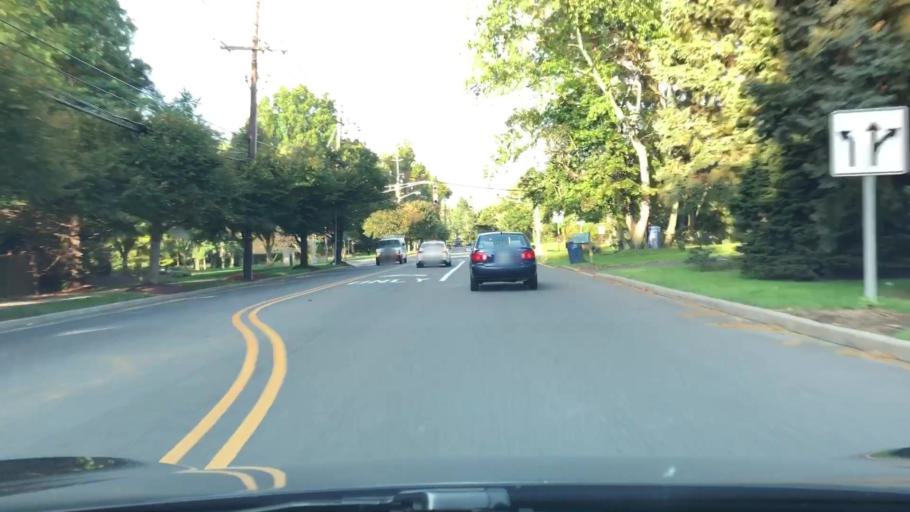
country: US
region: New Jersey
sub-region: Mercer County
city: Lawrenceville
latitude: 40.2895
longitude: -74.7576
